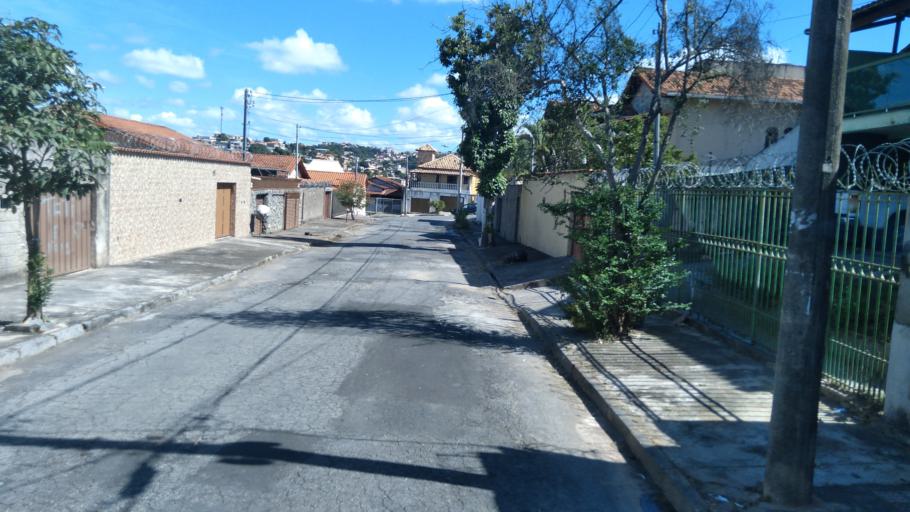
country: BR
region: Minas Gerais
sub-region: Belo Horizonte
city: Belo Horizonte
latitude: -19.8486
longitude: -43.9132
